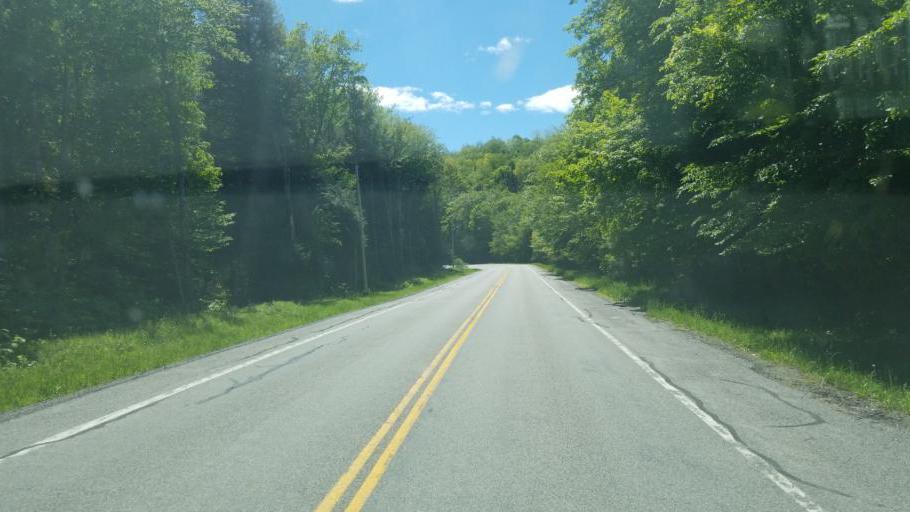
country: US
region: New York
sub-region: Montgomery County
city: Saint Johnsville
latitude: 43.1825
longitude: -74.5585
